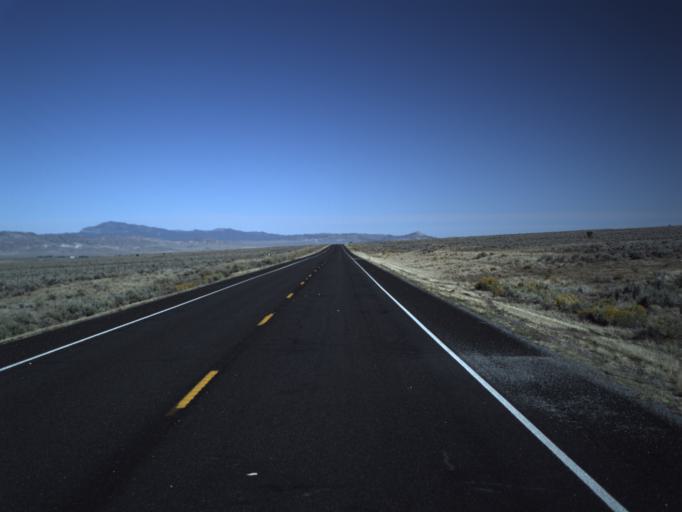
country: US
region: Utah
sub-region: Beaver County
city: Milford
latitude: 38.2424
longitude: -112.9400
